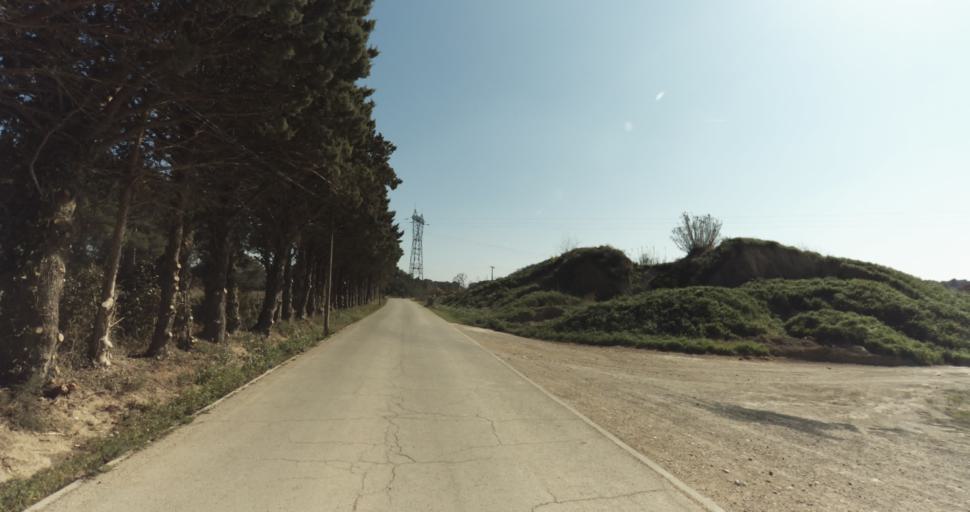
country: FR
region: Provence-Alpes-Cote d'Azur
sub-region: Departement des Bouches-du-Rhone
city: Pelissanne
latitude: 43.6449
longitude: 5.1647
